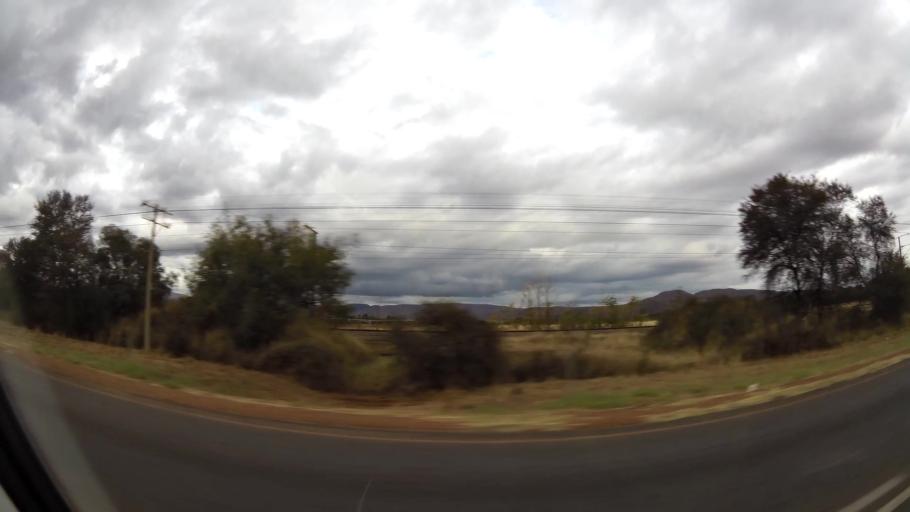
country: ZA
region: Limpopo
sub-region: Waterberg District Municipality
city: Mokopane
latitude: -24.2664
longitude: 28.9832
